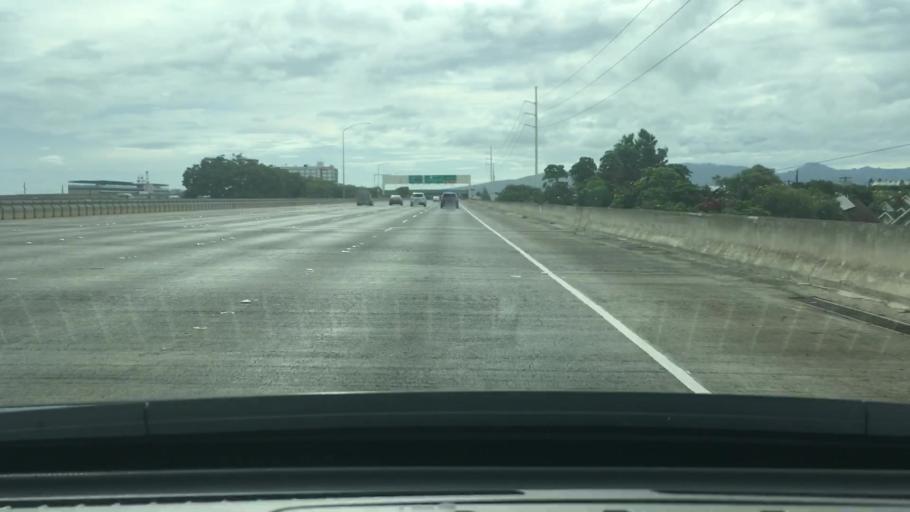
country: US
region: Hawaii
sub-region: Honolulu County
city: Halawa Heights
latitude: 21.3363
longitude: -157.9071
